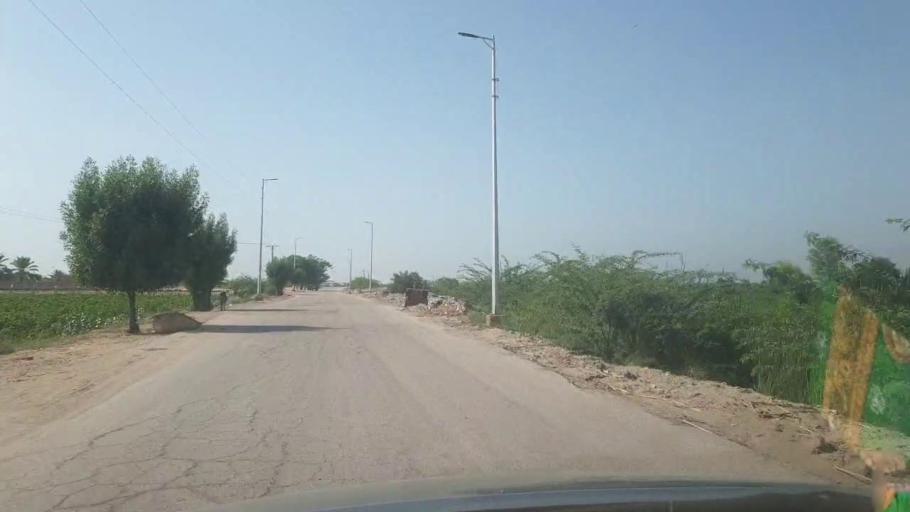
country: PK
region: Sindh
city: Rohri
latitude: 27.5078
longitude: 69.0366
